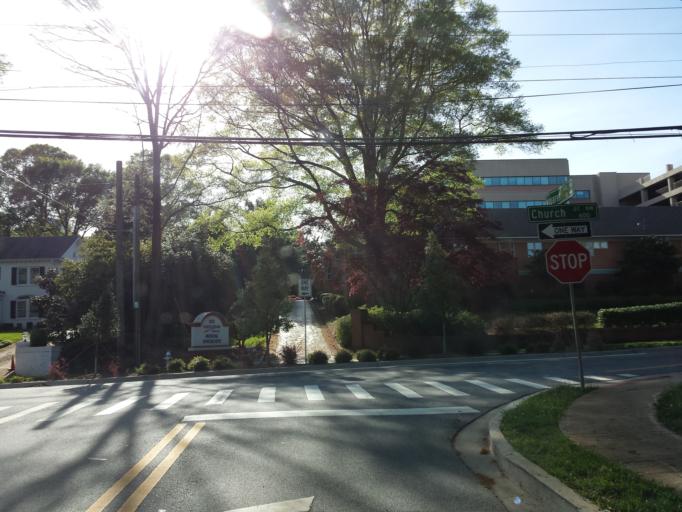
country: US
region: Georgia
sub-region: Cobb County
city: Marietta
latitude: 33.9665
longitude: -84.5498
